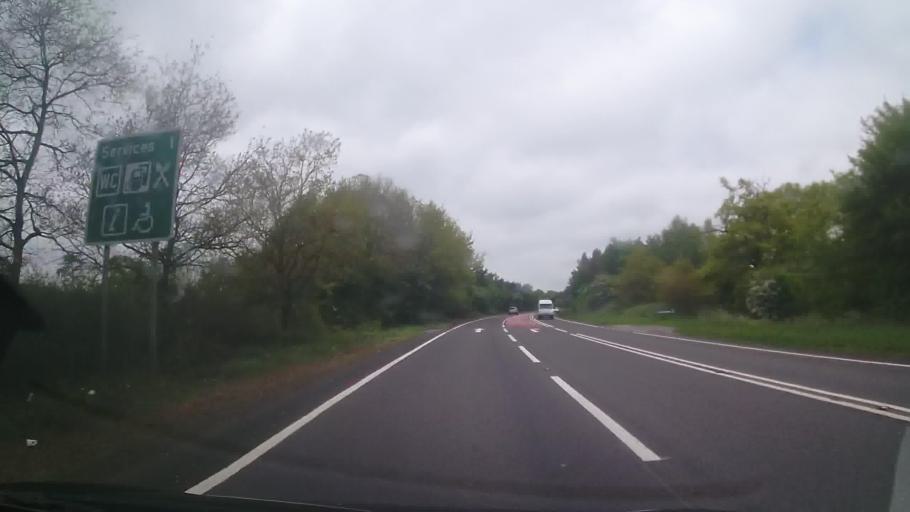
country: GB
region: England
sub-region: Shropshire
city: Whitchurch
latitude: 52.9569
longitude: -2.6906
